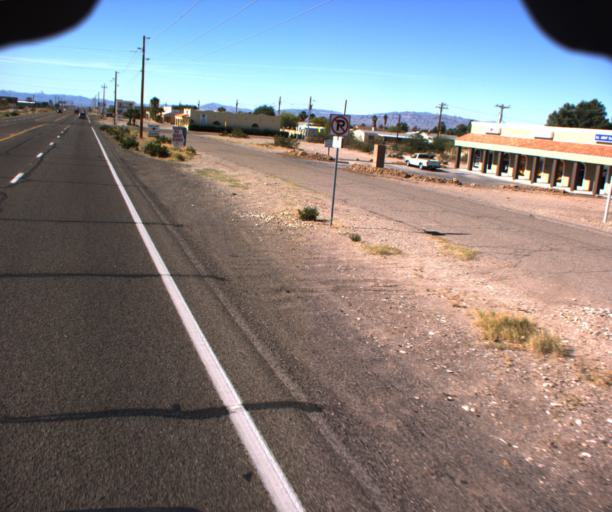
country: US
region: Arizona
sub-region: Mohave County
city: Mohave Valley
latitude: 34.9945
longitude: -114.5981
